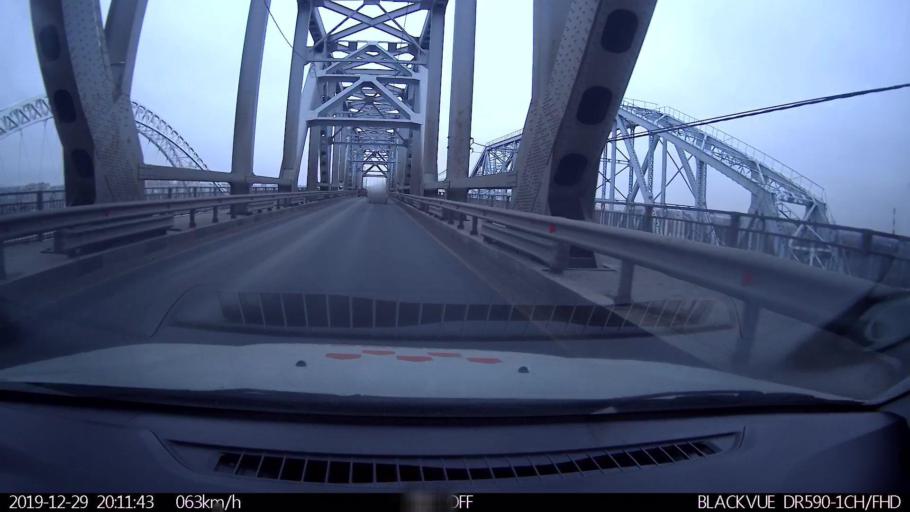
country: RU
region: Nizjnij Novgorod
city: Neklyudovo
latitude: 56.3542
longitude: 43.9248
